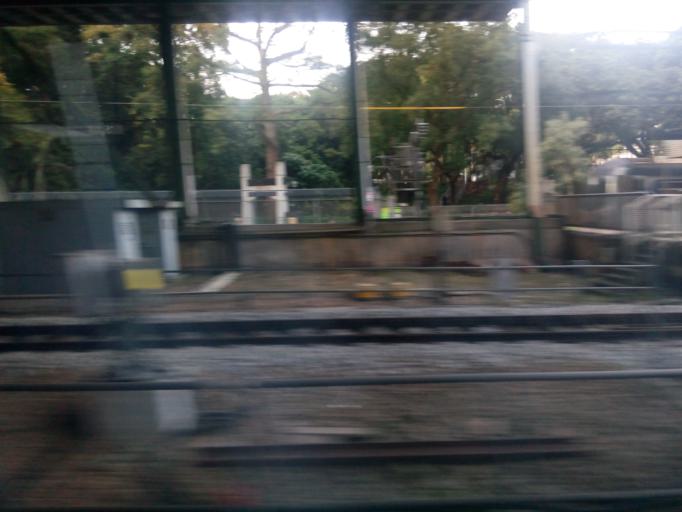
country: HK
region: Tai Po
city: Tai Po
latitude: 22.4446
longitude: 114.1695
